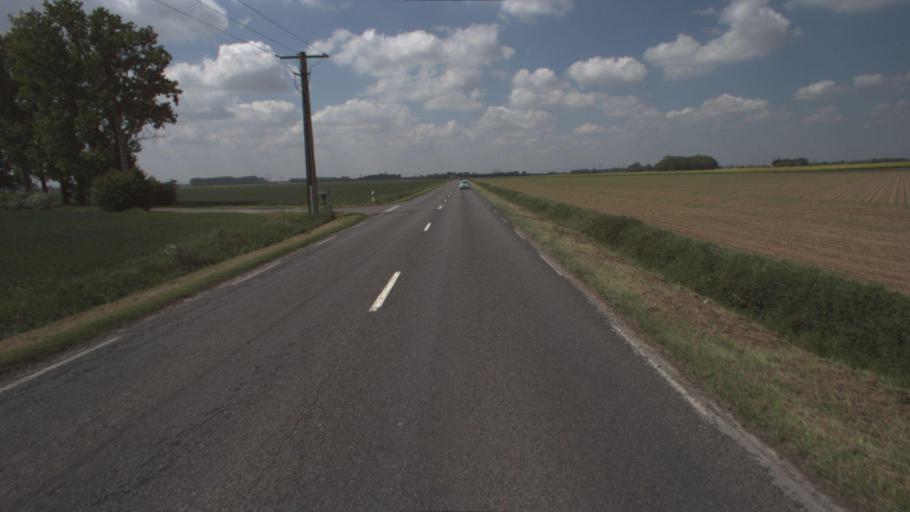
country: FR
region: Ile-de-France
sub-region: Departement de Seine-et-Marne
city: Guignes
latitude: 48.6226
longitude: 2.7634
